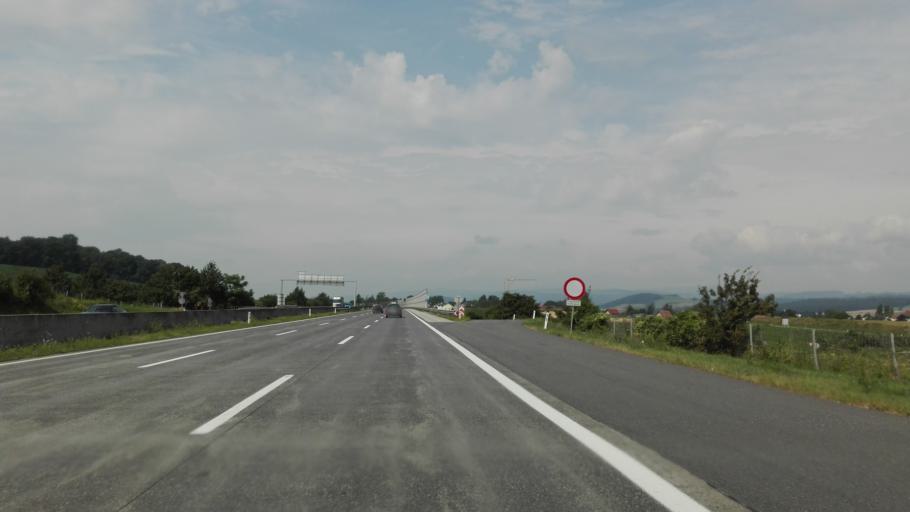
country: AT
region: Lower Austria
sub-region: Politischer Bezirk Melk
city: Melk
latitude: 48.2175
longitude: 15.3342
